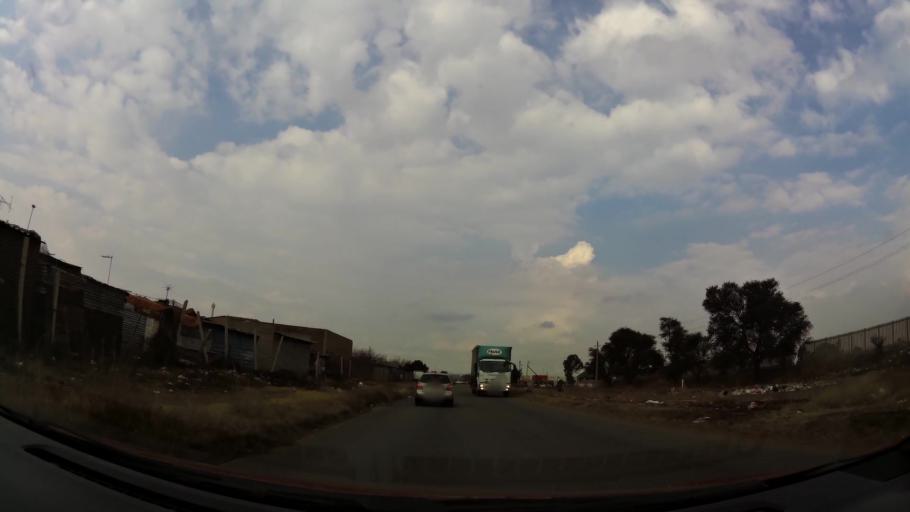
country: ZA
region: Gauteng
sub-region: Sedibeng District Municipality
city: Vanderbijlpark
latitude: -26.6658
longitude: 27.8622
